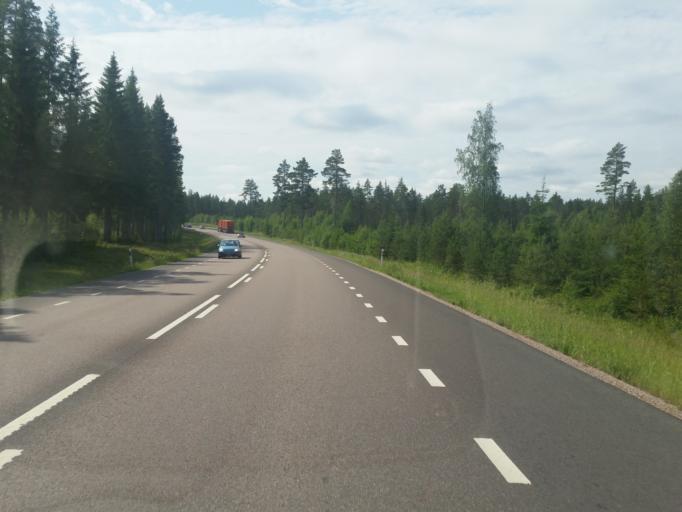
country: SE
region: Dalarna
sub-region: Gagnefs Kommun
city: Gagnef
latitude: 60.6443
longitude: 15.0591
